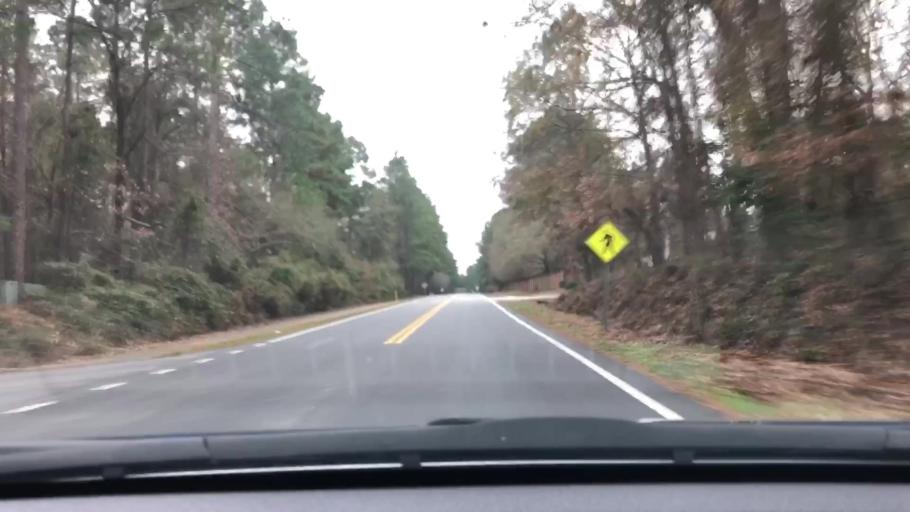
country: US
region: South Carolina
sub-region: Sumter County
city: Cherryvale
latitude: 33.9431
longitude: -80.4038
